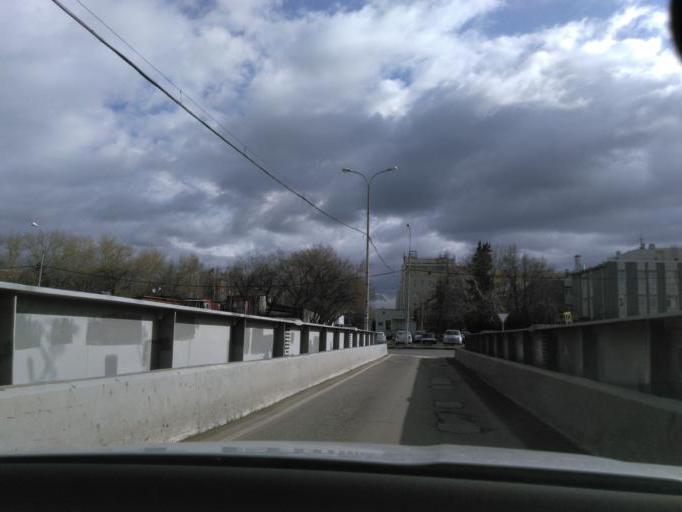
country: RU
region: Moscow
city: Novyye Cheremushki
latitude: 55.6949
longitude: 37.5973
